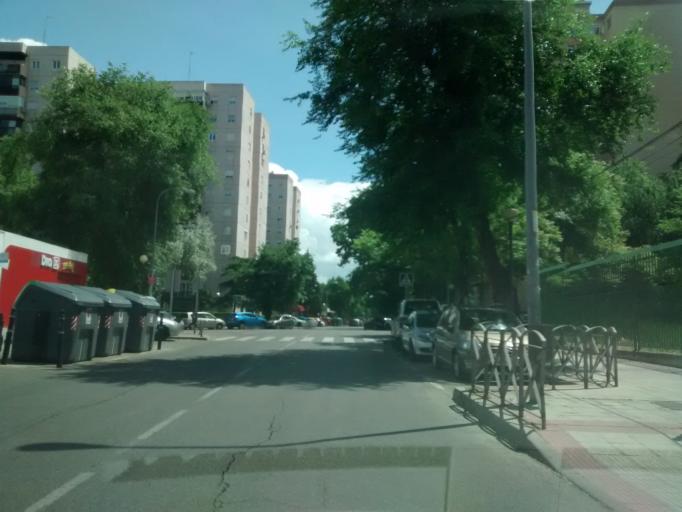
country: ES
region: Madrid
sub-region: Provincia de Madrid
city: San Fernando de Henares
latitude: 40.4275
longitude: -3.5402
